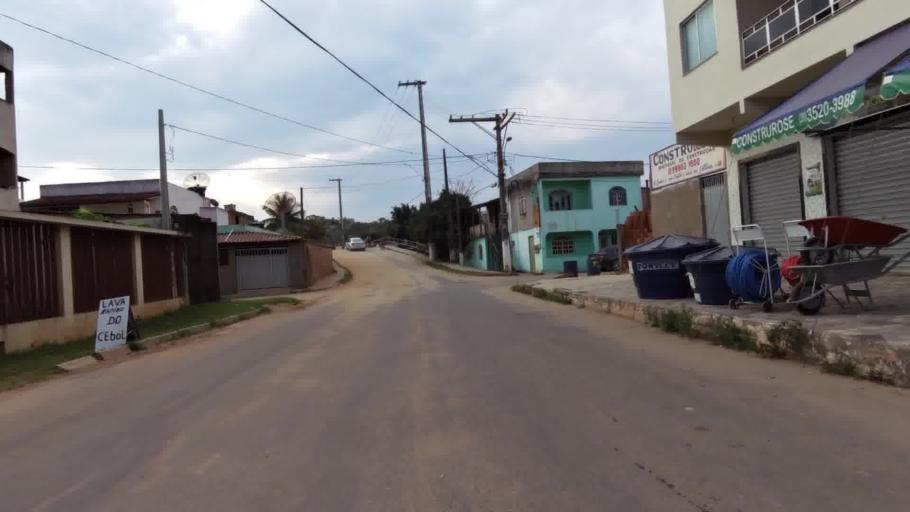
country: BR
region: Espirito Santo
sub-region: Piuma
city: Piuma
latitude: -20.8415
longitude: -40.7448
